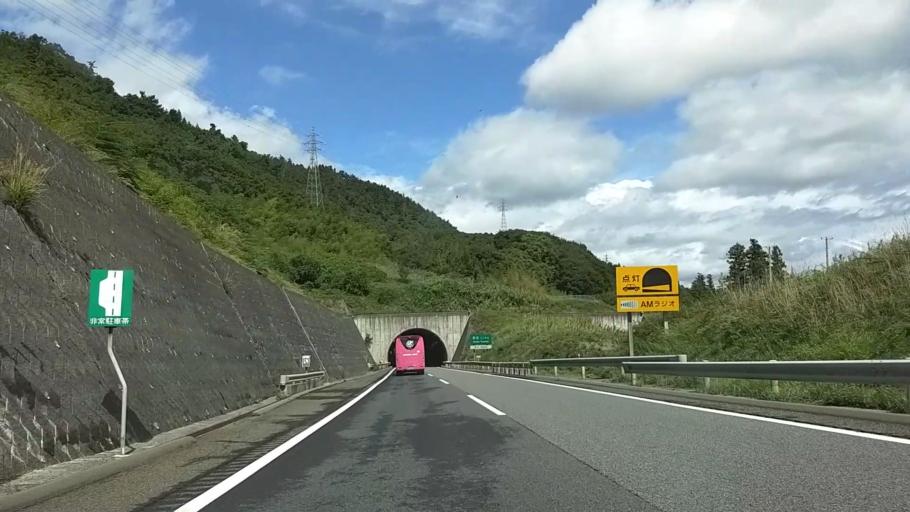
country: JP
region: Nagano
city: Nagano-shi
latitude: 36.5435
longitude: 138.0977
